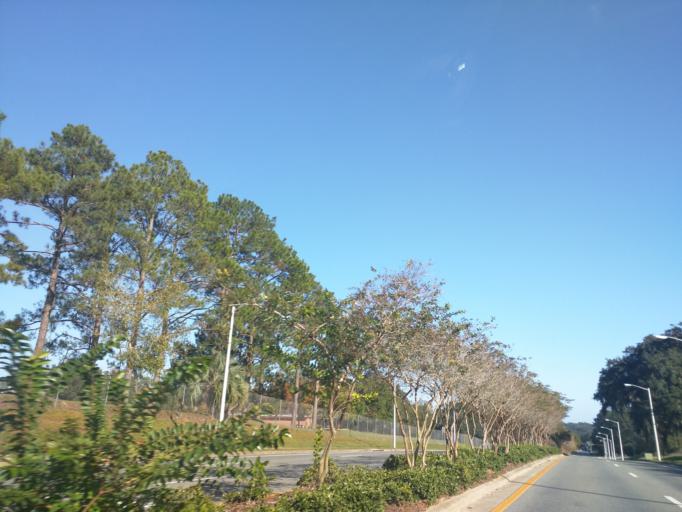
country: US
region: Florida
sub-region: Leon County
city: Tallahassee
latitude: 30.4401
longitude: -84.2224
